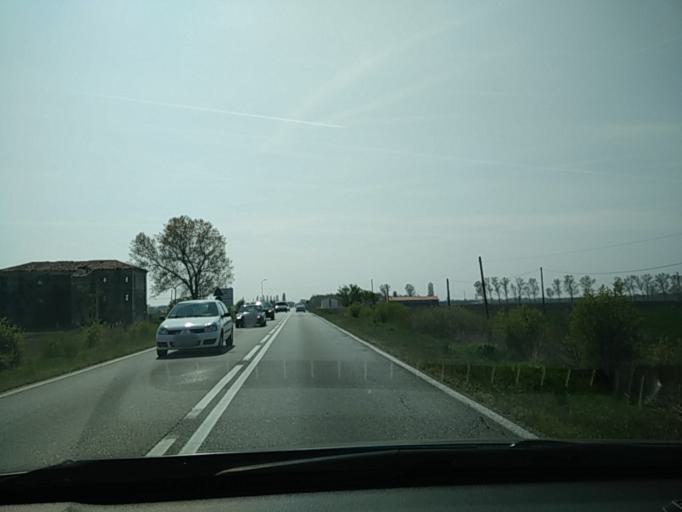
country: IT
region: Veneto
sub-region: Provincia di Venezia
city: Ceggia
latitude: 45.6704
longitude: 12.6218
